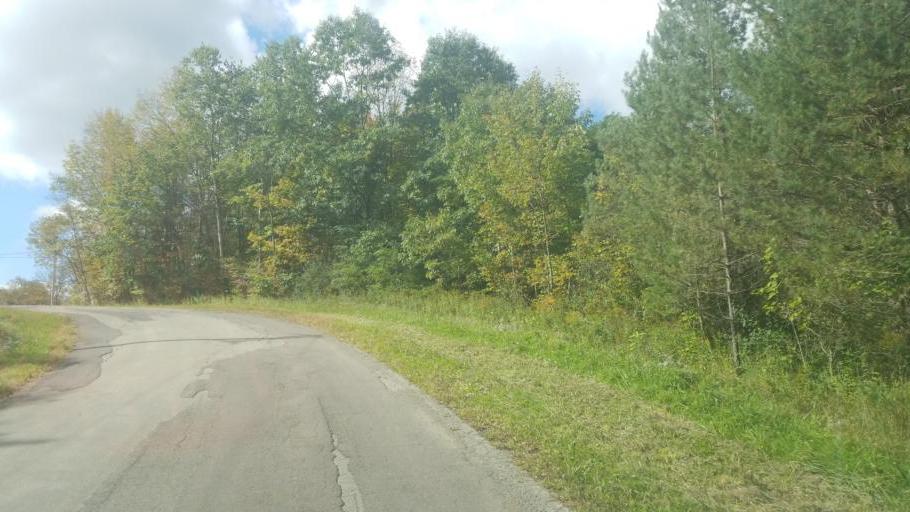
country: US
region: New York
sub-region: Cattaraugus County
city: Franklinville
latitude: 42.2282
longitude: -78.4151
